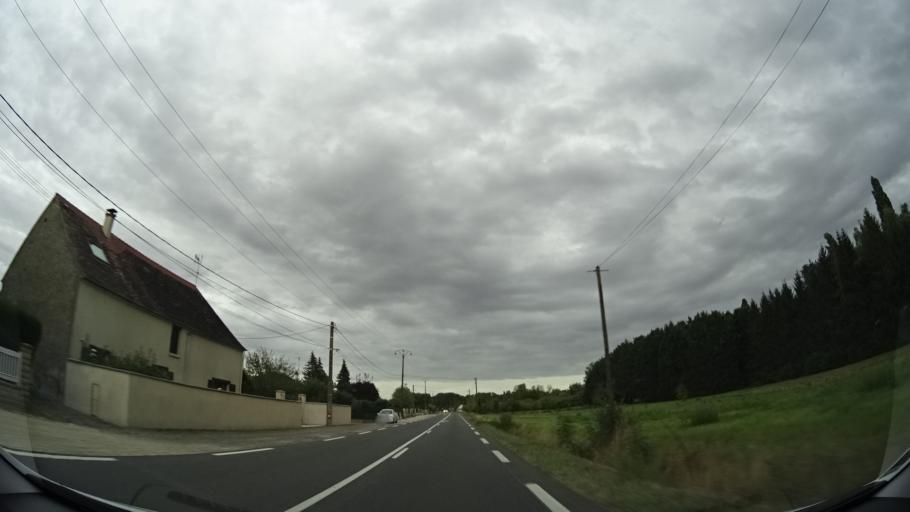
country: FR
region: Centre
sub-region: Departement du Loiret
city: Saint-Germain-des-Pres
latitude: 47.9565
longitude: 2.8096
